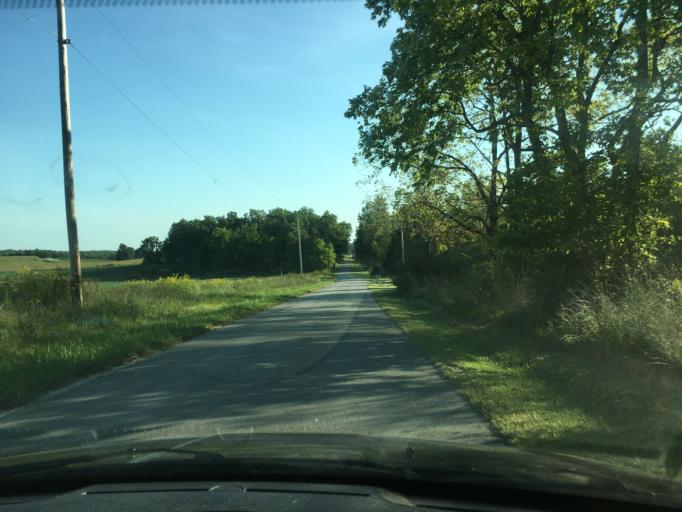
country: US
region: Ohio
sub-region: Logan County
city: West Liberty
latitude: 40.2444
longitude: -83.6673
